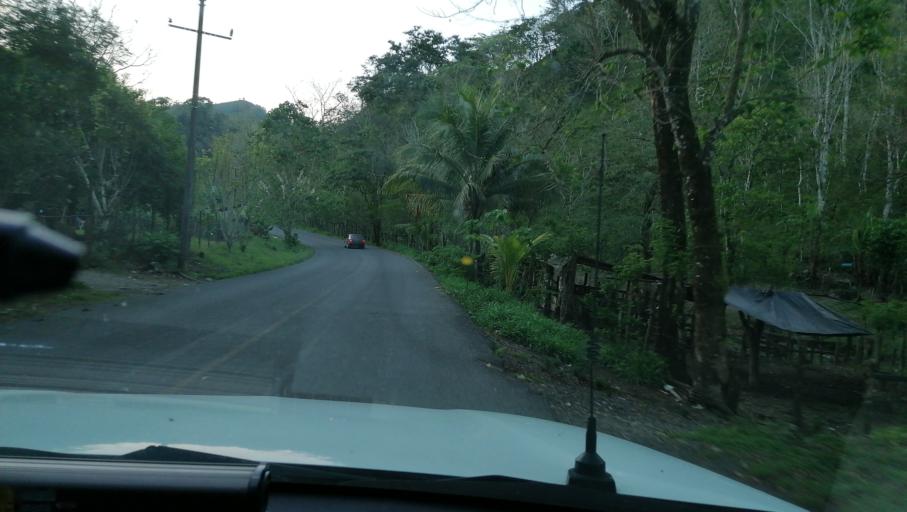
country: MX
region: Chiapas
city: Ostuacan
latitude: 17.4157
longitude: -93.3389
